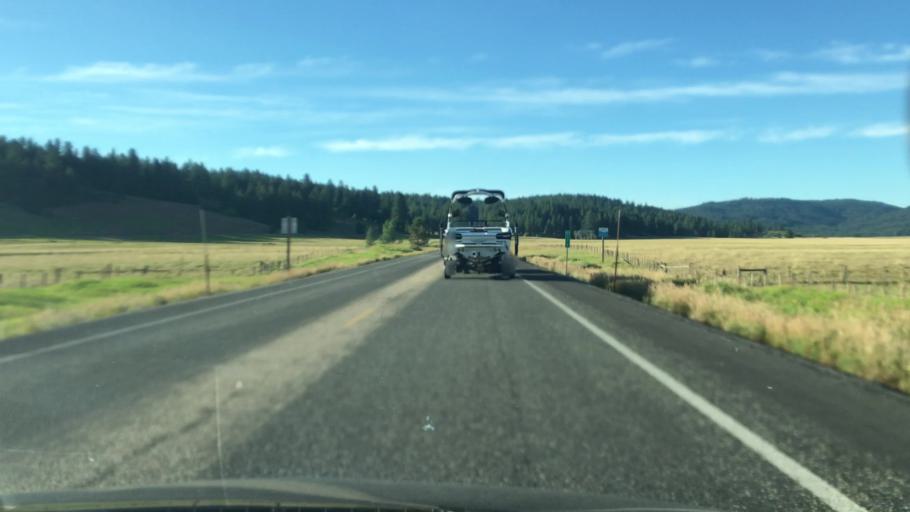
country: US
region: Idaho
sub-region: Valley County
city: Cascade
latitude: 44.5500
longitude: -116.0272
